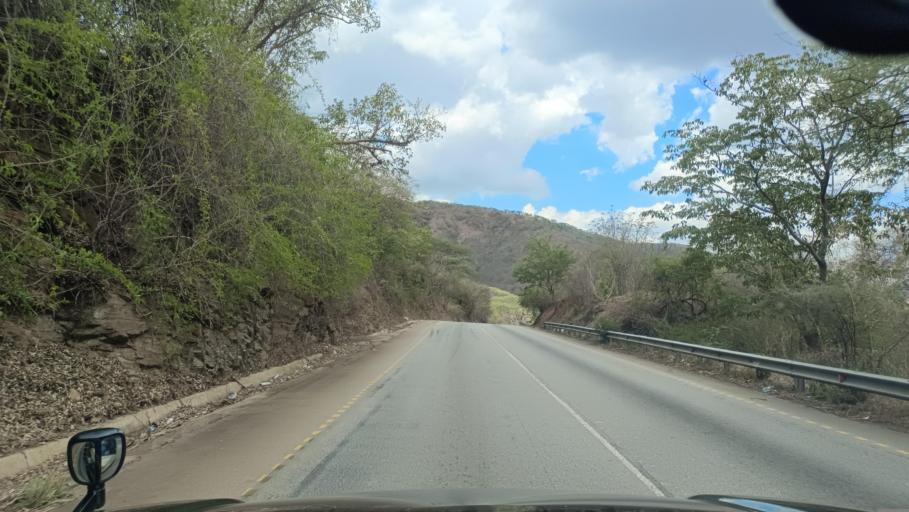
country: TZ
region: Morogoro
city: Kidatu
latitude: -7.5757
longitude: 36.7494
